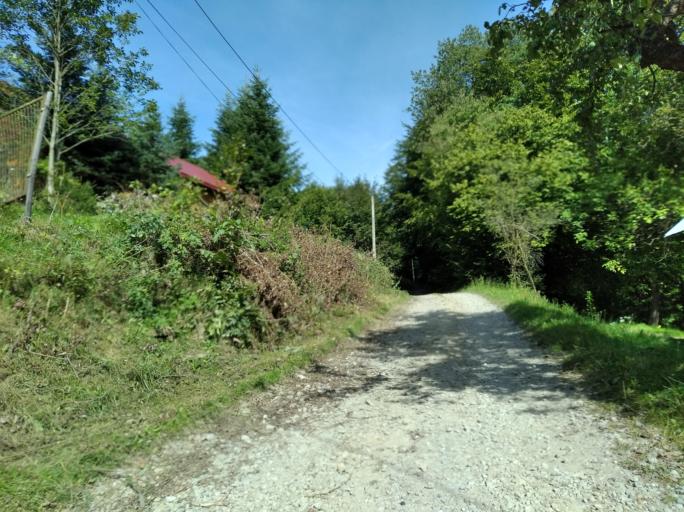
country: PL
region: Subcarpathian Voivodeship
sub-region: Powiat ropczycko-sedziszowski
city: Wielopole Skrzynskie
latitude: 49.9107
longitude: 21.6239
